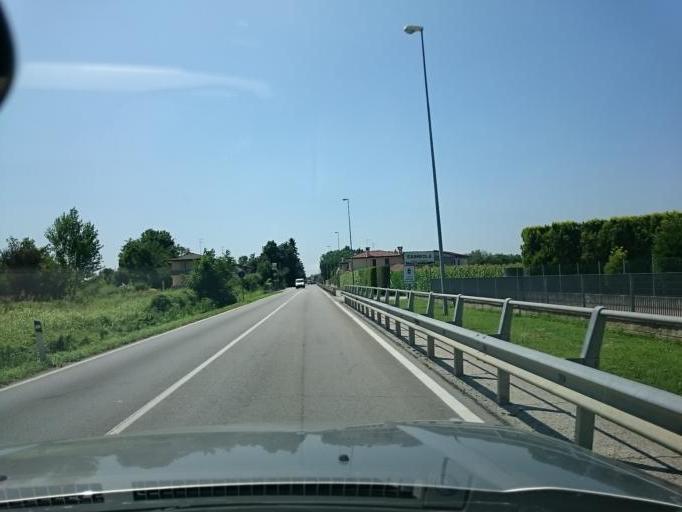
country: IT
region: Veneto
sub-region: Provincia di Padova
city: Villaguattera
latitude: 45.4343
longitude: 11.8274
